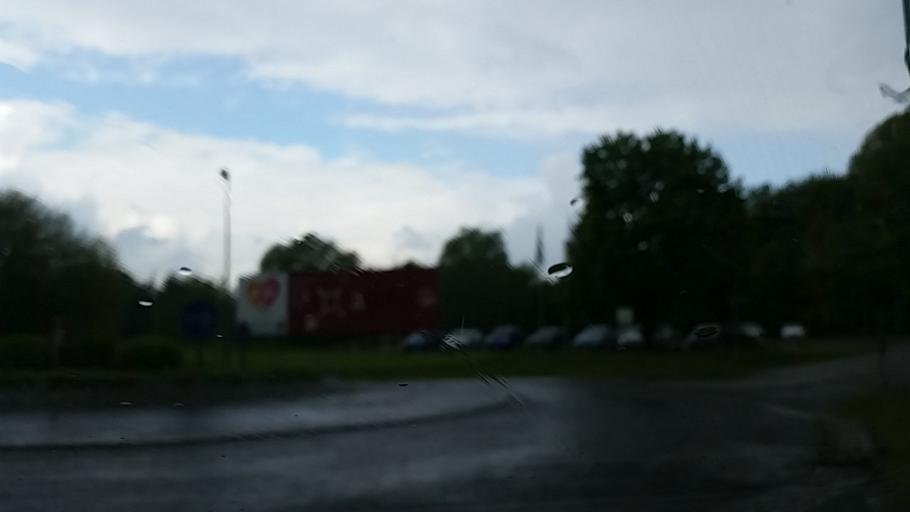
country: DE
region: Brandenburg
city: Diensdorf-Radlow
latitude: 52.2494
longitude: 14.0283
